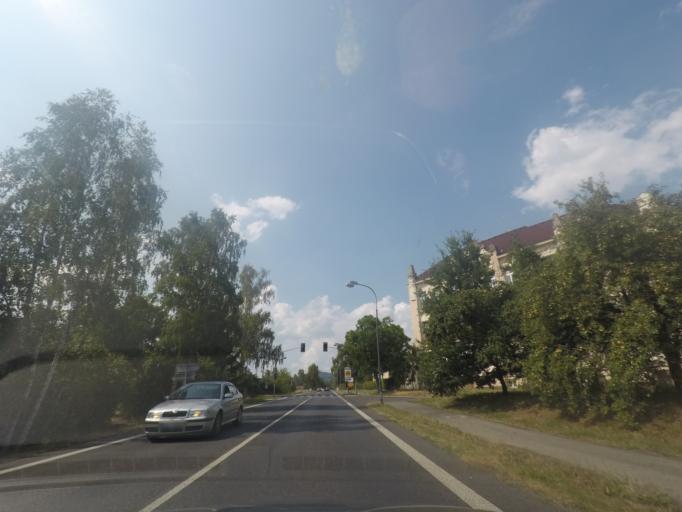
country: CZ
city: Cvikov
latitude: 50.7753
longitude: 14.6295
